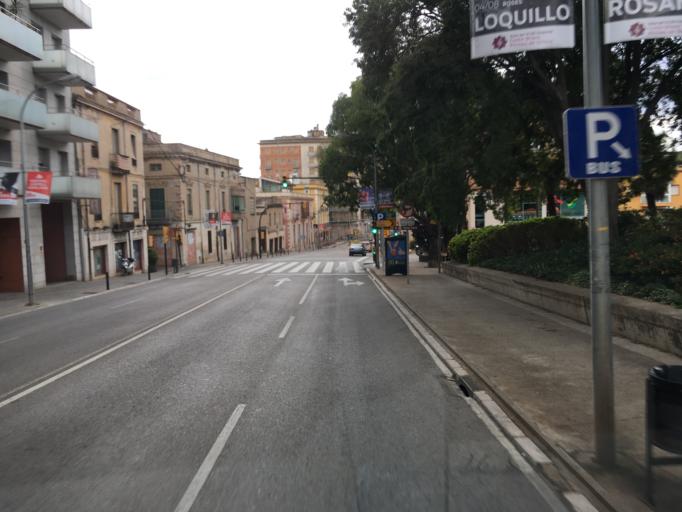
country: ES
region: Catalonia
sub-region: Provincia de Girona
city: Figueres
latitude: 42.2671
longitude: 2.9579
